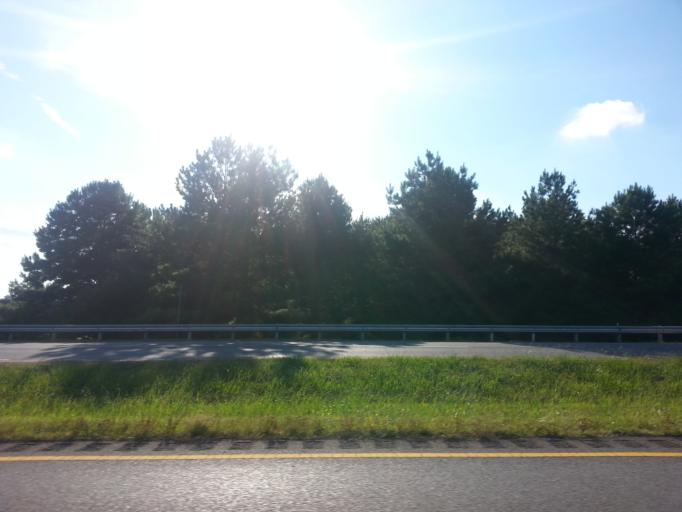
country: US
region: Alabama
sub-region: Colbert County
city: Muscle Shoals
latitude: 34.7231
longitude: -87.6678
